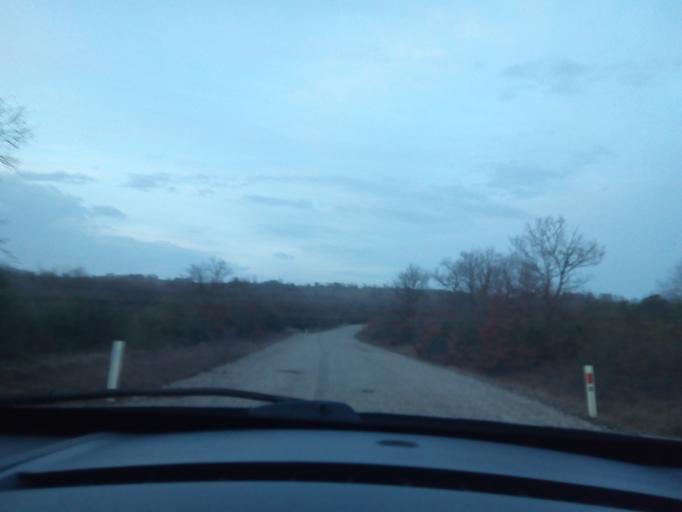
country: TR
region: Balikesir
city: Omerkoy
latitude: 39.9012
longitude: 28.0291
